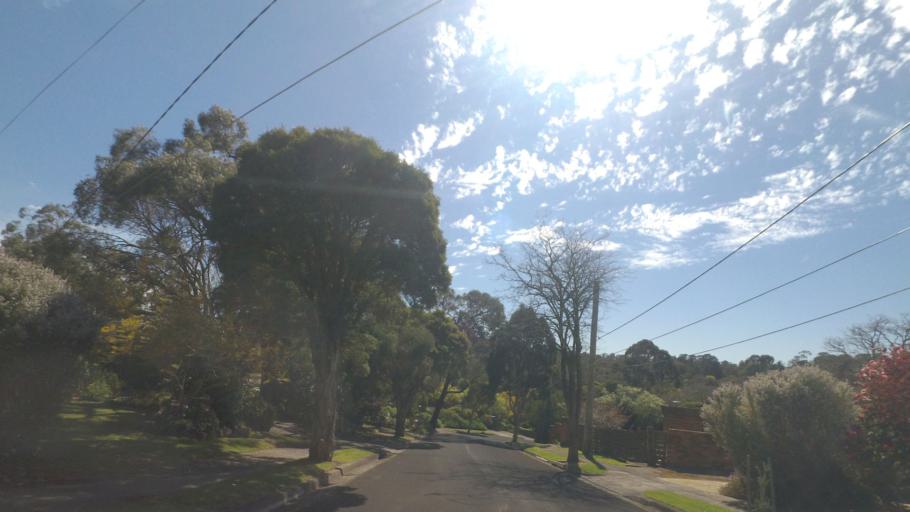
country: AU
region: Victoria
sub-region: Maroondah
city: Croydon South
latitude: -37.8137
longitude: 145.2595
